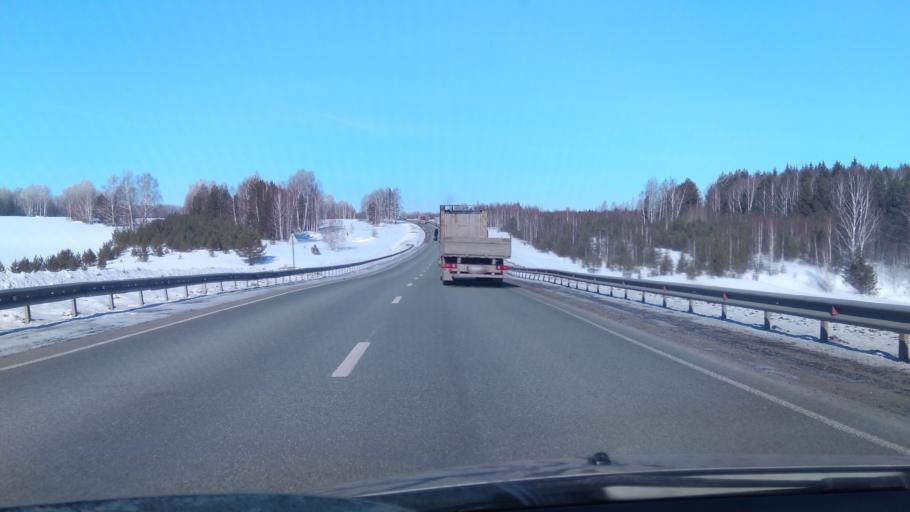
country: RU
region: Perm
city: Suksun
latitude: 56.9259
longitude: 57.5596
